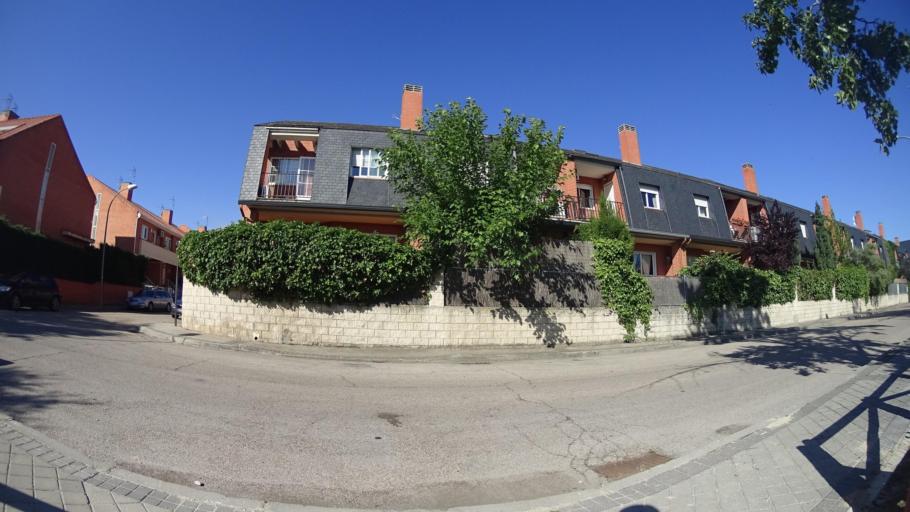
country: ES
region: Madrid
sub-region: Provincia de Madrid
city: Las Matas
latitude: 40.5513
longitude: -3.8878
